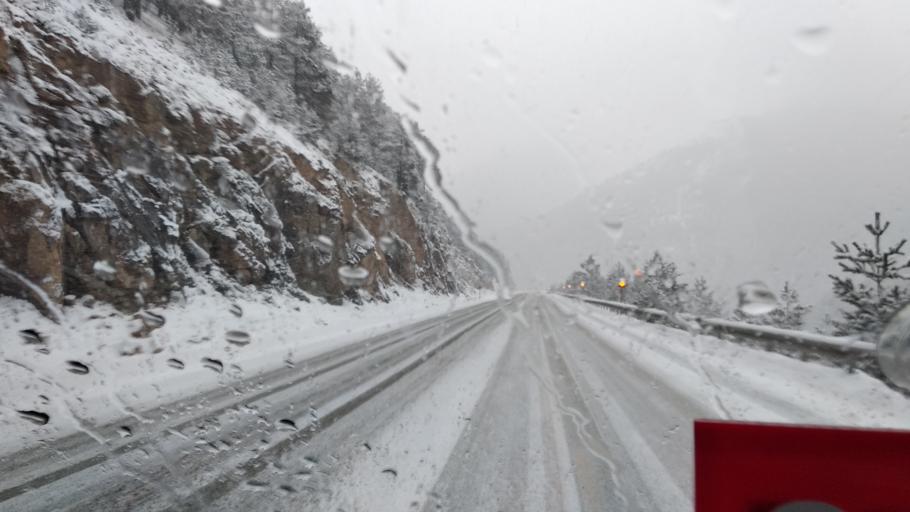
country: TR
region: Gumushane
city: Torul
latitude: 40.6563
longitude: 39.4071
